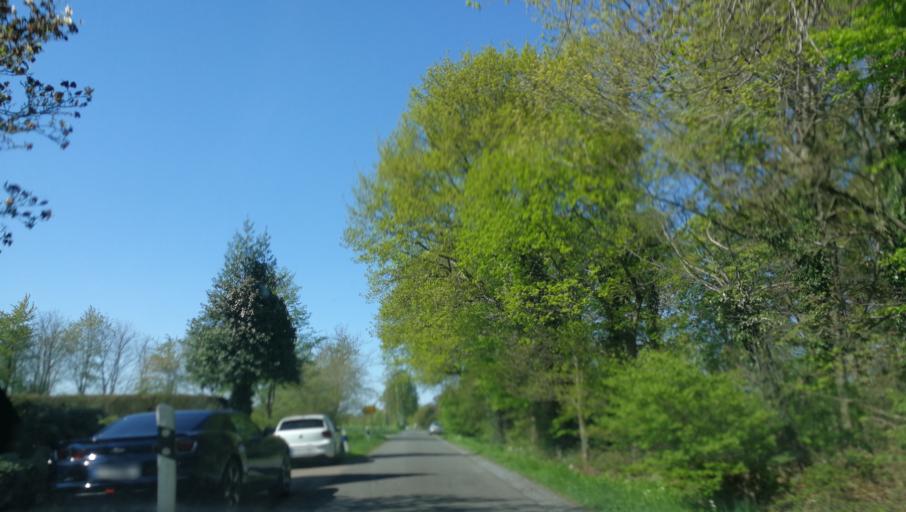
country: DE
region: North Rhine-Westphalia
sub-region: Regierungsbezirk Munster
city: Muenster
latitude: 51.9303
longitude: 7.5601
